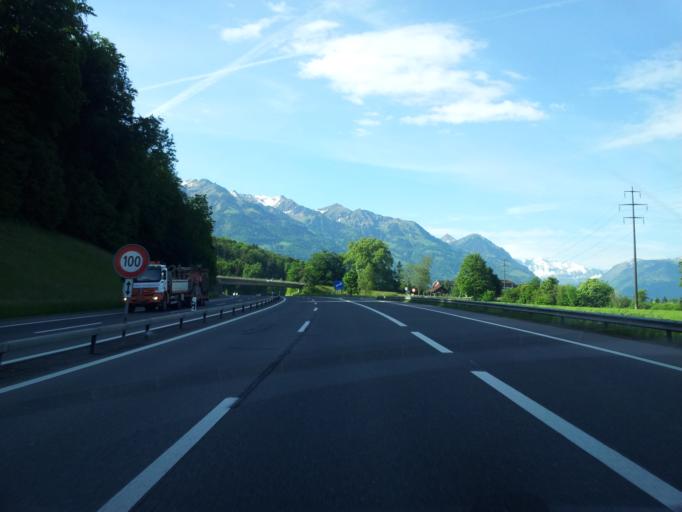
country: CH
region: Obwalden
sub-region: Obwalden
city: Sarnen
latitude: 46.8994
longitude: 8.2579
